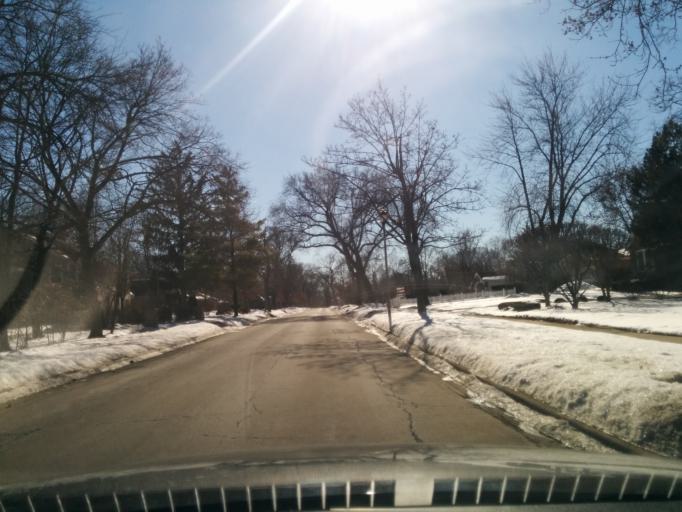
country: US
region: Illinois
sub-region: DuPage County
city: Elmhurst
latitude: 41.8922
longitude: -87.9368
